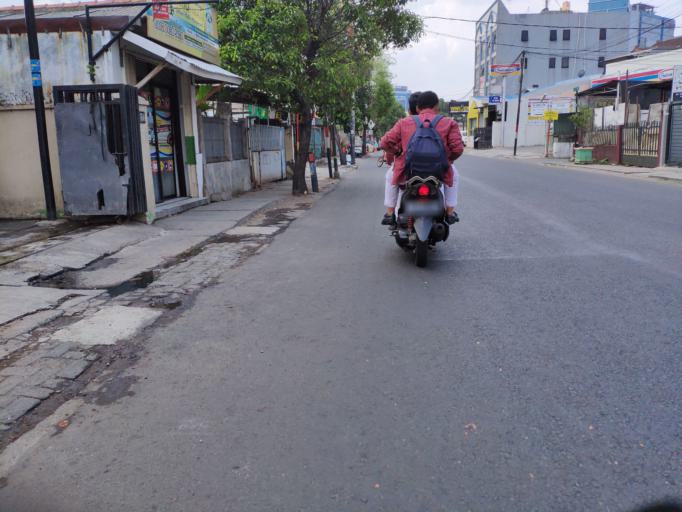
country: ID
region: Jakarta Raya
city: Jakarta
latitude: -6.1959
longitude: 106.8701
